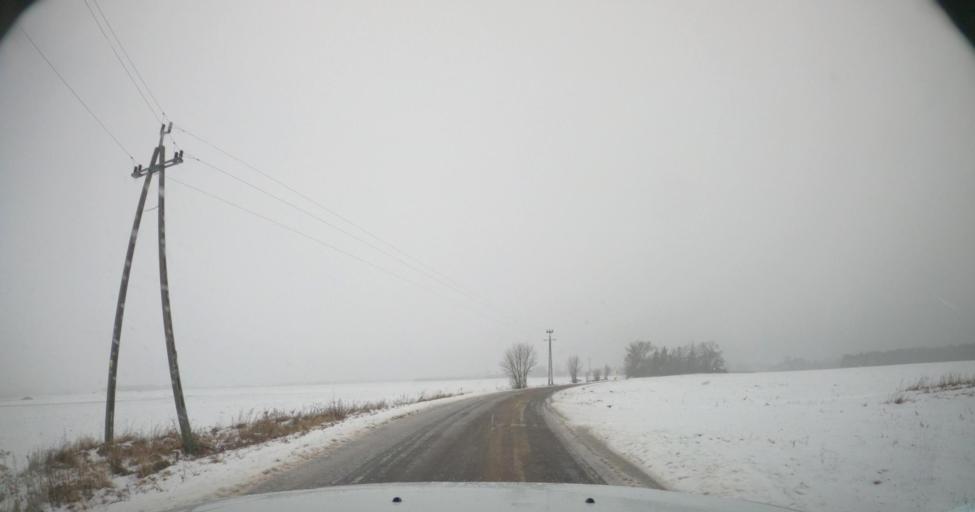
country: PL
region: West Pomeranian Voivodeship
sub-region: Powiat kamienski
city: Golczewo
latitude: 53.8030
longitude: 14.9674
